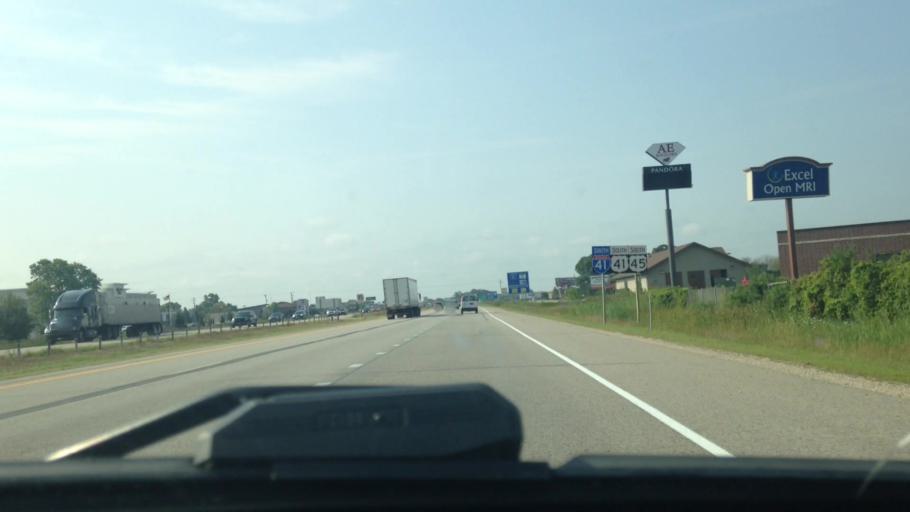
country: US
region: Wisconsin
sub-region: Fond du Lac County
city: North Fond du Lac
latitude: 43.7813
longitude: -88.4827
